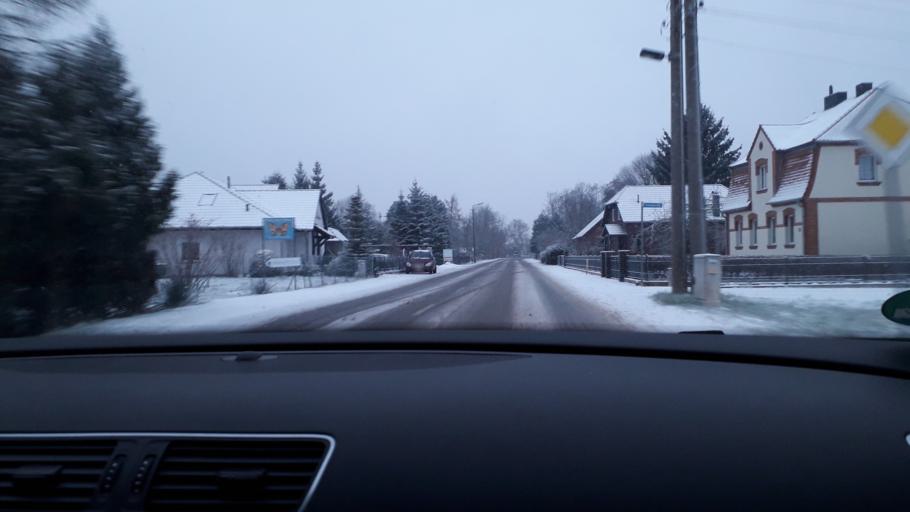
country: DE
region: Brandenburg
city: Spremberg
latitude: 51.5819
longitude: 14.4079
